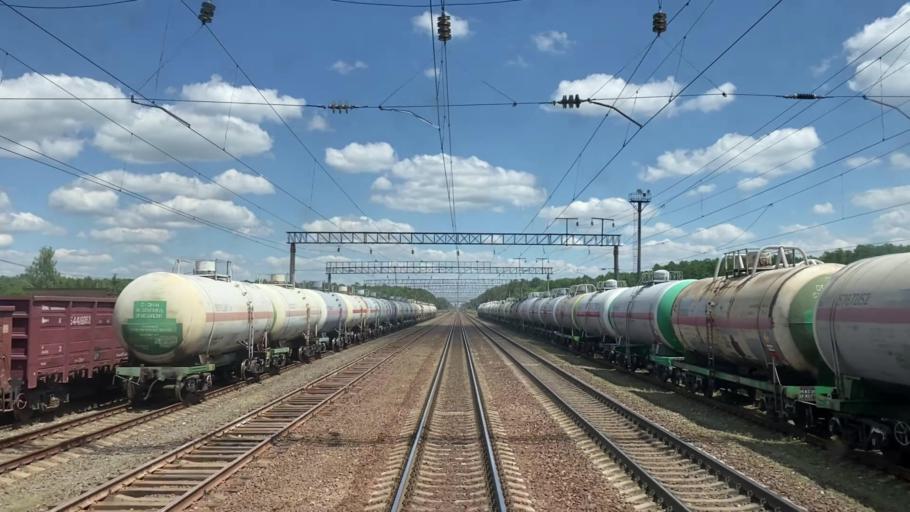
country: BY
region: Brest
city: Pruzhany
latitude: 52.4747
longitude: 24.5365
